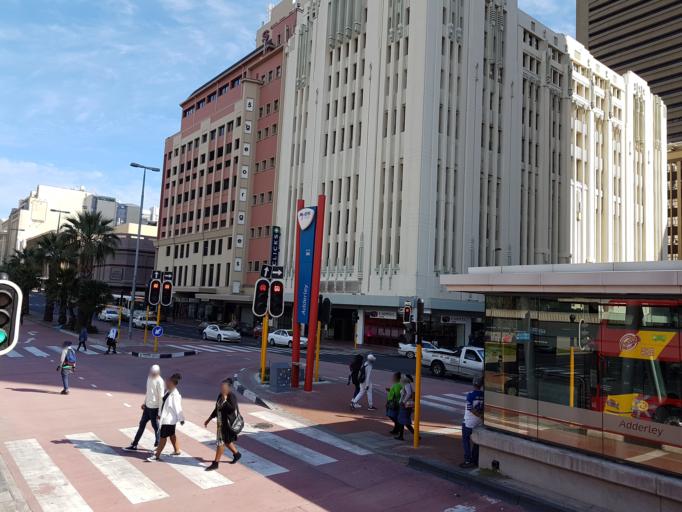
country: ZA
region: Western Cape
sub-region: City of Cape Town
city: Cape Town
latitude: -33.9209
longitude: 18.4247
